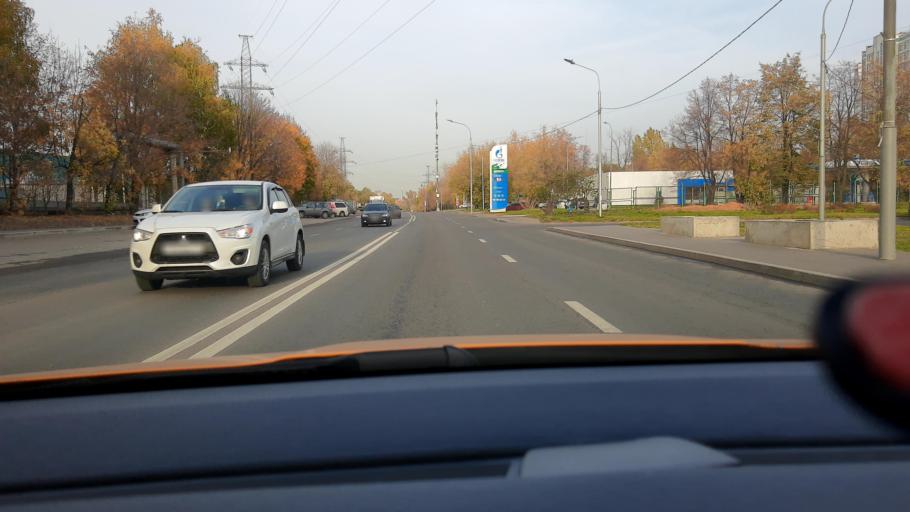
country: RU
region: Moscow
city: Businovo
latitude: 55.8946
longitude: 37.5233
